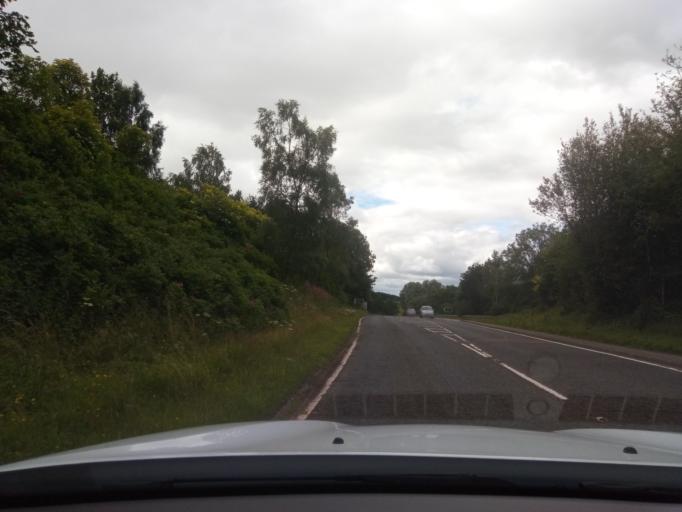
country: GB
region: Scotland
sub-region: Stirling
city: Dunblane
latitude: 56.1918
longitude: -3.9824
